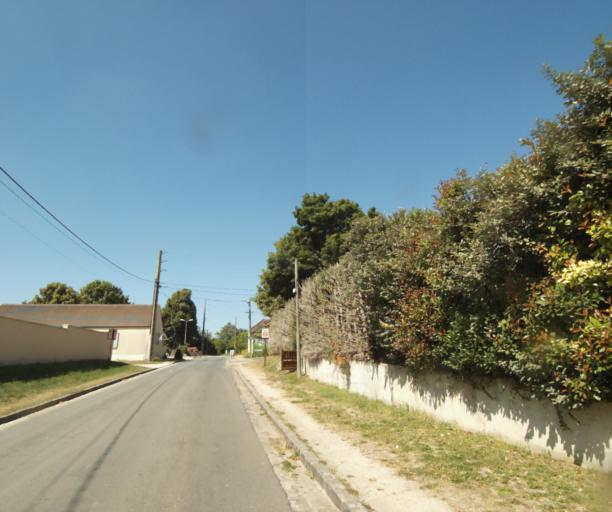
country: FR
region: Ile-de-France
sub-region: Departement de Seine-et-Marne
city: Acheres-la-Foret
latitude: 48.3474
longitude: 2.5641
